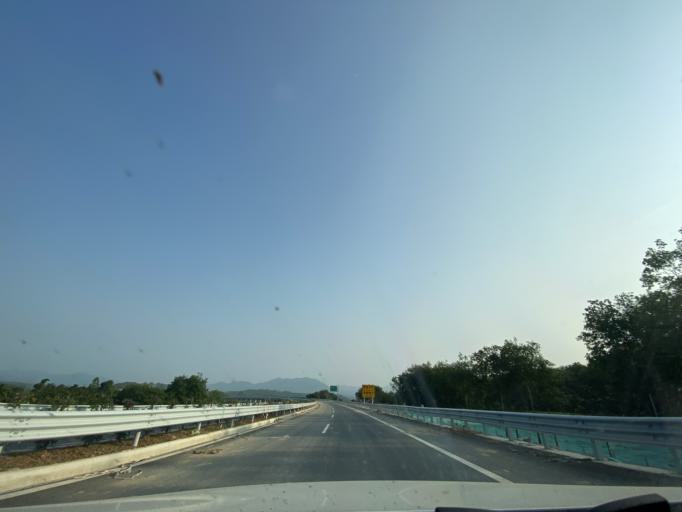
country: CN
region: Hainan
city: Xiangshui
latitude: 18.6410
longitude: 109.6291
